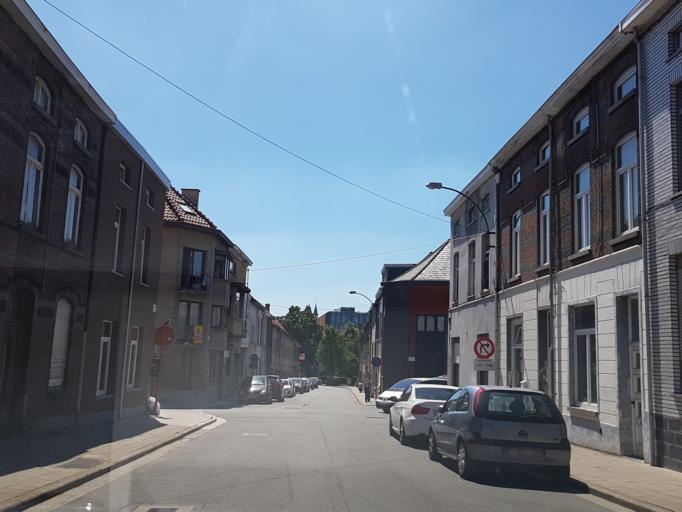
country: BE
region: Flanders
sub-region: Provincie Oost-Vlaanderen
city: Aalst
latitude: 50.9439
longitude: 4.0434
